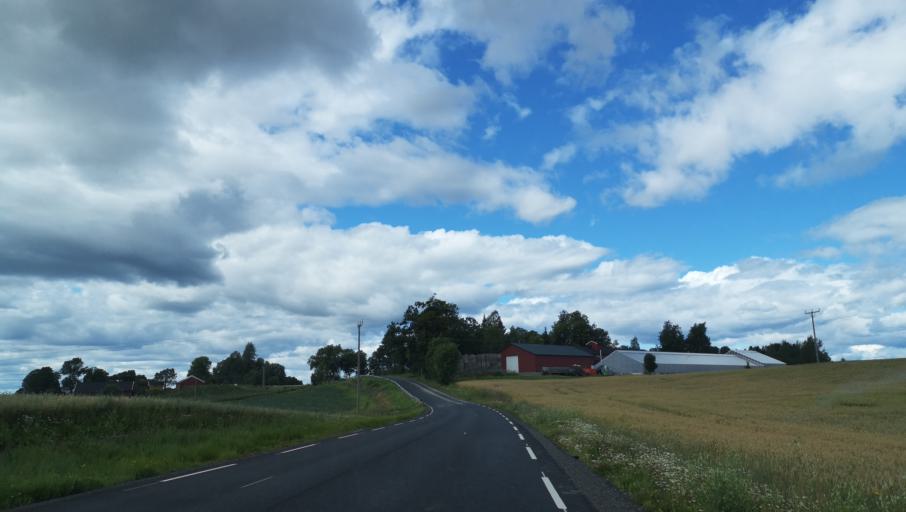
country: NO
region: Akershus
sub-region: Ski
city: Ski
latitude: 59.6928
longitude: 10.9083
